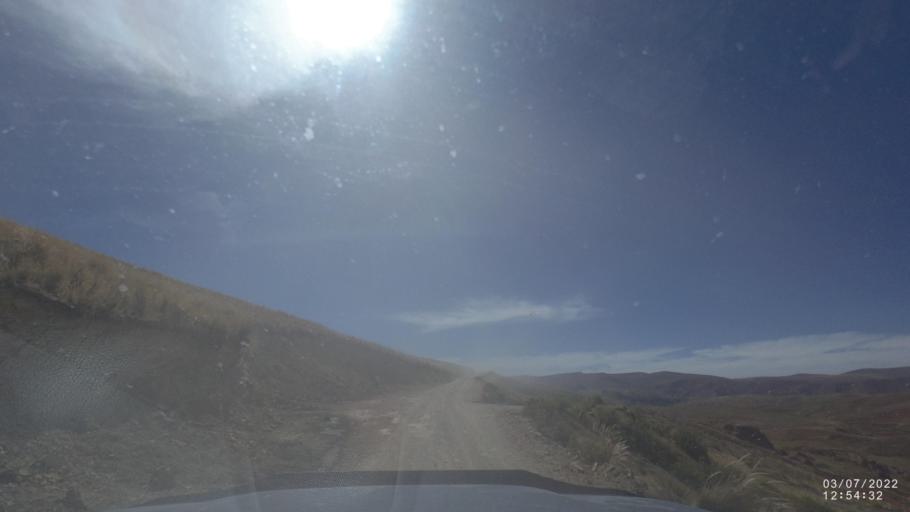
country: BO
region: Cochabamba
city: Irpa Irpa
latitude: -17.7388
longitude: -66.6681
